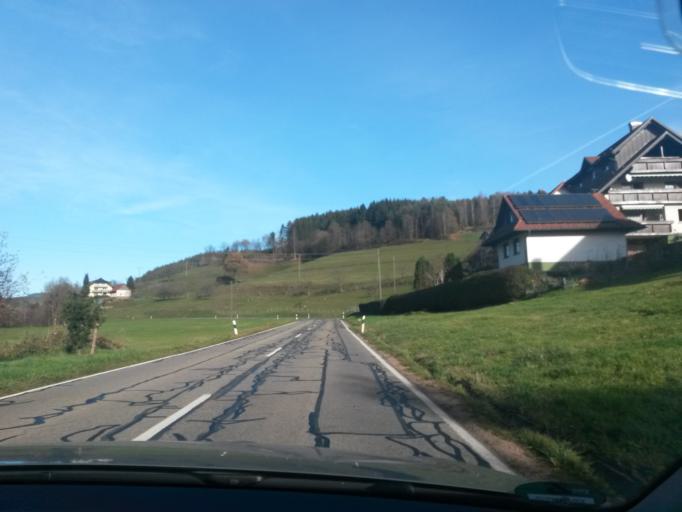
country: DE
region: Baden-Wuerttemberg
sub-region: Freiburg Region
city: Elzach
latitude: 48.1882
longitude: 8.0856
